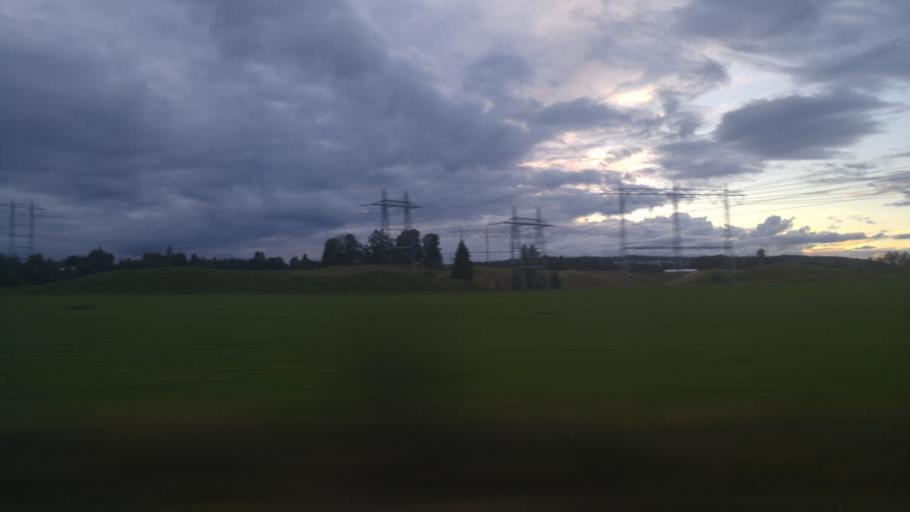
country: NO
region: Akershus
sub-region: Skedsmo
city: Leirsund
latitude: 60.0073
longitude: 11.0984
